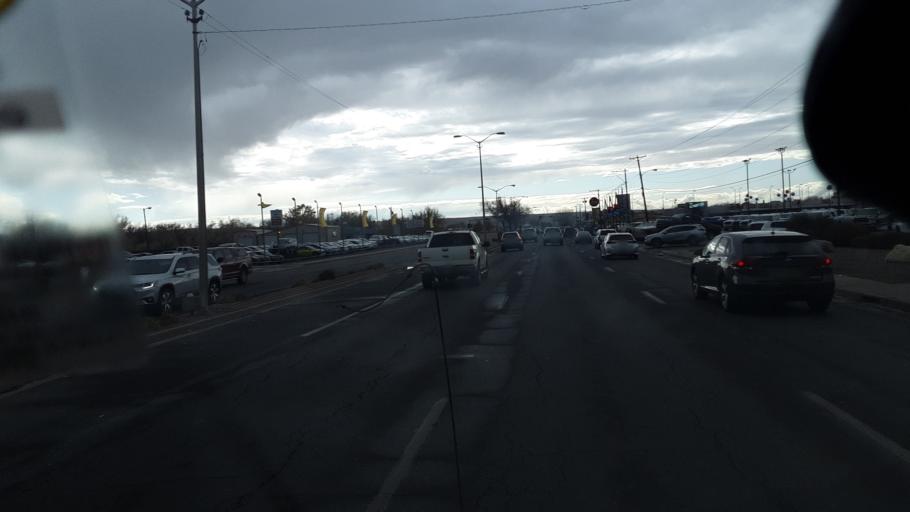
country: US
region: New Mexico
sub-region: San Juan County
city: Farmington
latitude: 36.7492
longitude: -108.1605
